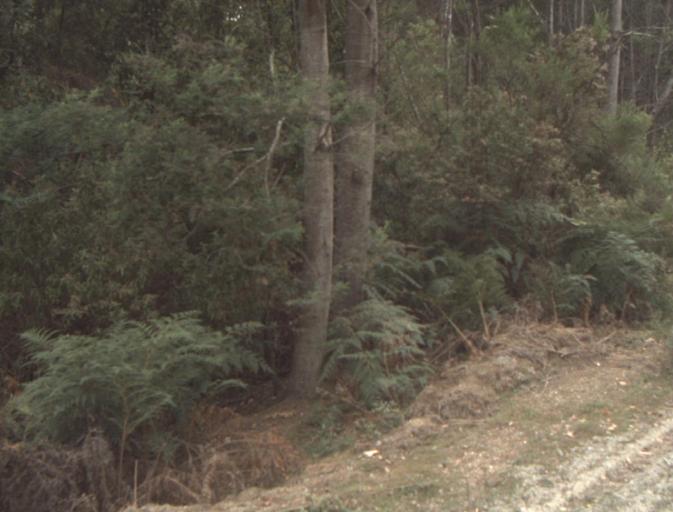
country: AU
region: Tasmania
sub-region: Launceston
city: Mayfield
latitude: -41.1706
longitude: 147.1950
